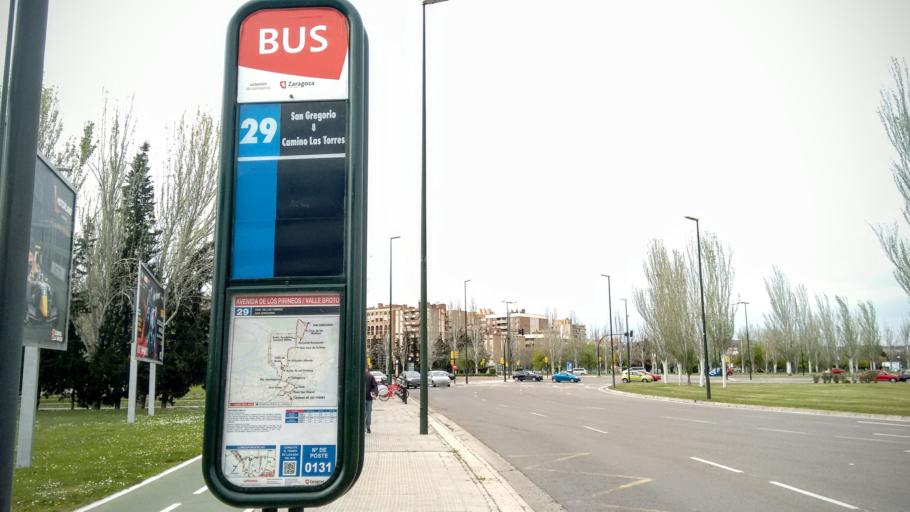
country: ES
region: Aragon
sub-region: Provincia de Zaragoza
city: Zaragoza
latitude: 41.6659
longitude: -0.8808
